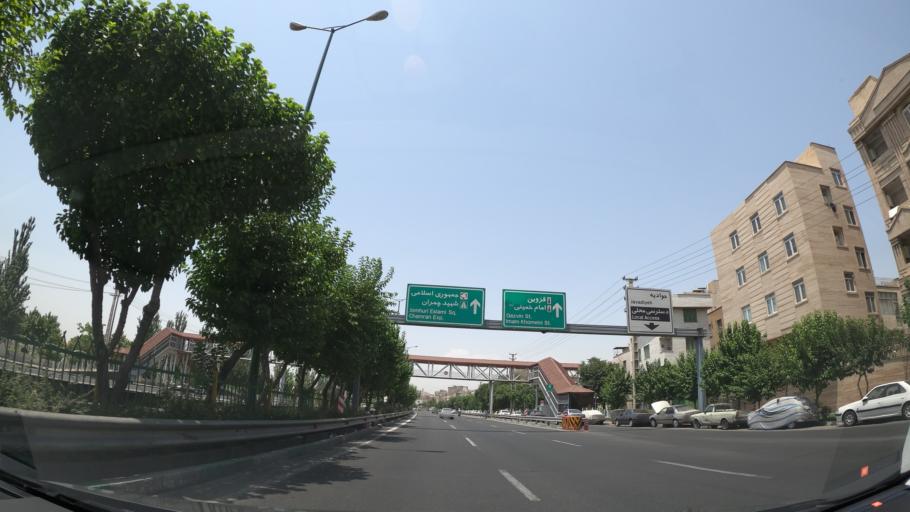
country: IR
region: Tehran
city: Tehran
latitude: 35.6487
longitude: 51.3901
